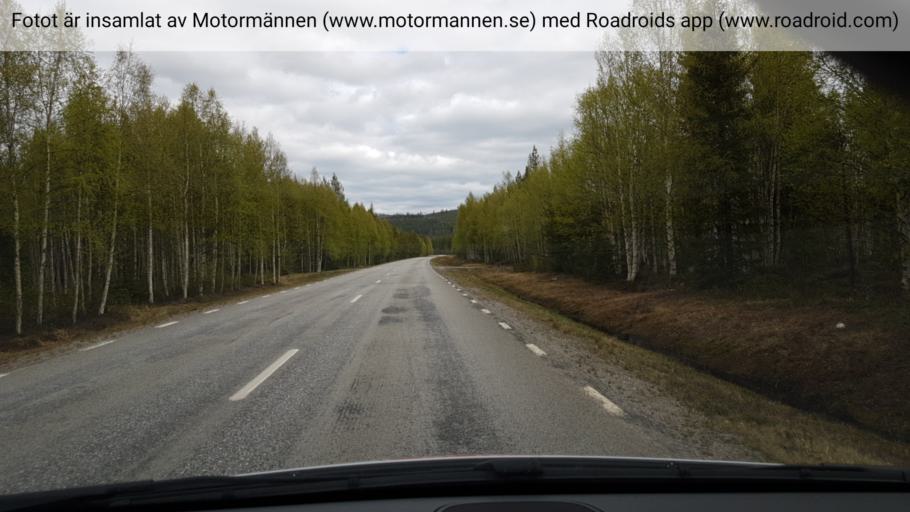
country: SE
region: Vaesterbotten
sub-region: Mala Kommun
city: Mala
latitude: 64.9325
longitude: 18.6200
